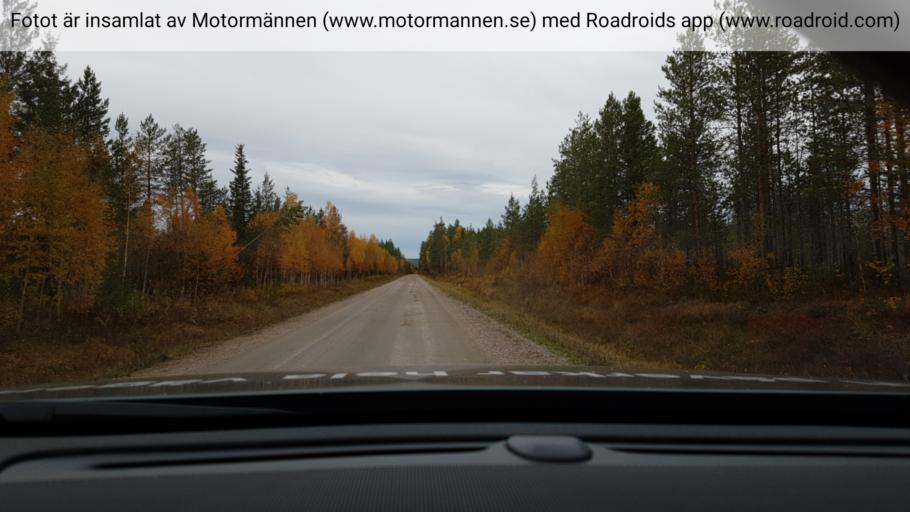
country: SE
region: Norrbotten
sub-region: Overkalix Kommun
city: OEverkalix
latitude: 66.2880
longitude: 22.9680
